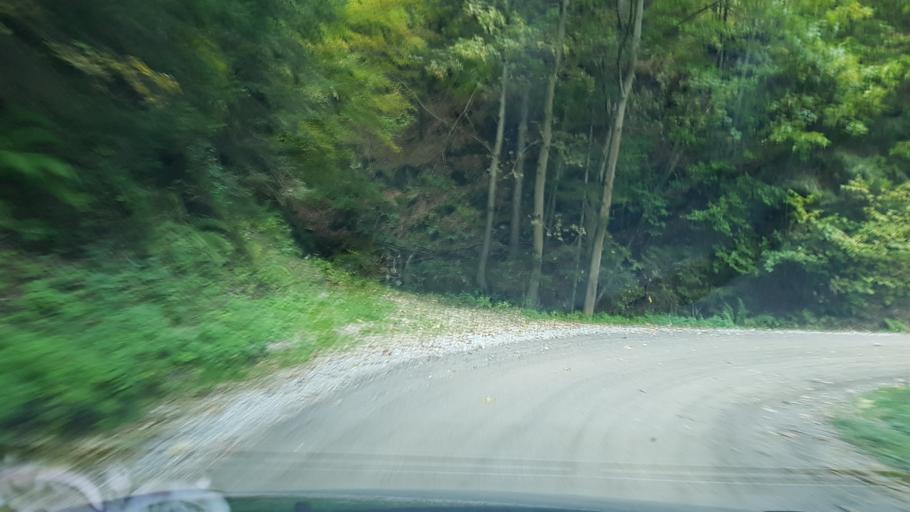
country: SI
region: Slovenj Gradec
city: Legen
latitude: 46.5207
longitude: 15.1324
